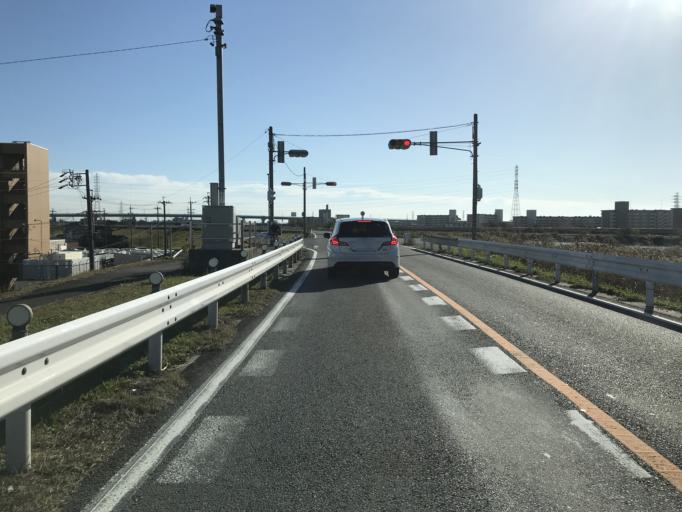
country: JP
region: Aichi
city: Kanie
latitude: 35.1653
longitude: 136.8356
